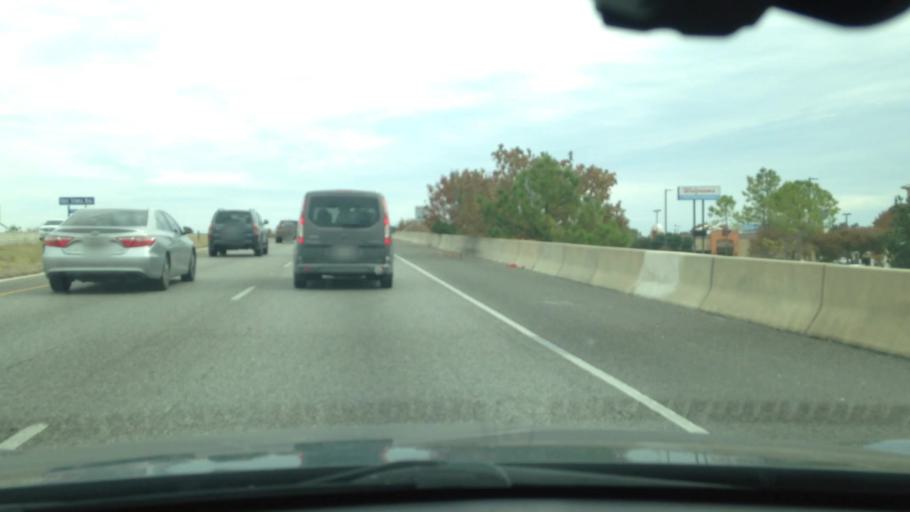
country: US
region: Texas
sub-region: Bastrop County
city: Bastrop
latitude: 30.1076
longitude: -97.3366
